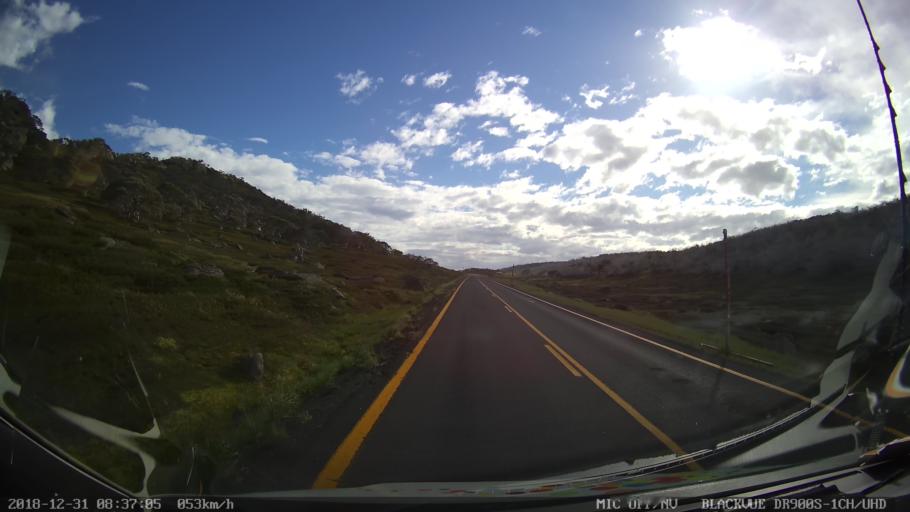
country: AU
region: New South Wales
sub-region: Snowy River
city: Jindabyne
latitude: -36.4209
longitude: 148.3820
